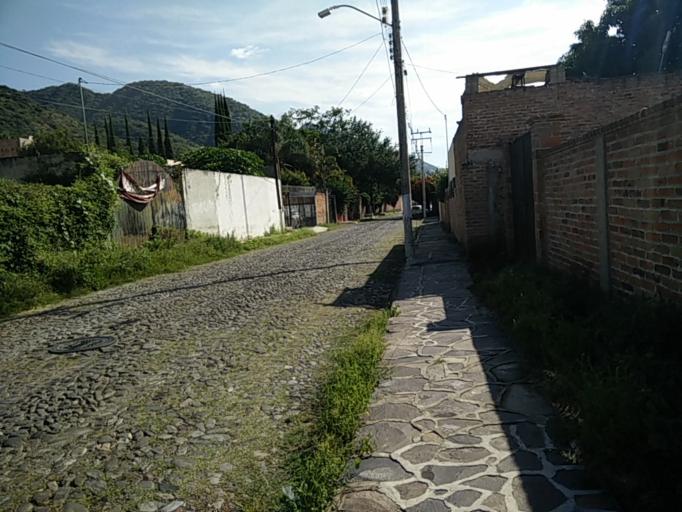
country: MX
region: Jalisco
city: Ajijic
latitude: 20.3004
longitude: -103.2750
